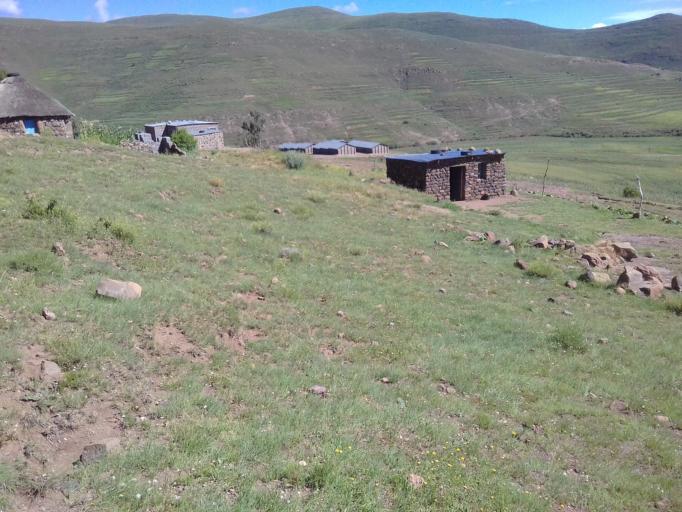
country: LS
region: Thaba-Tseka
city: Thaba-Tseka
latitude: -29.5249
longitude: 28.5844
